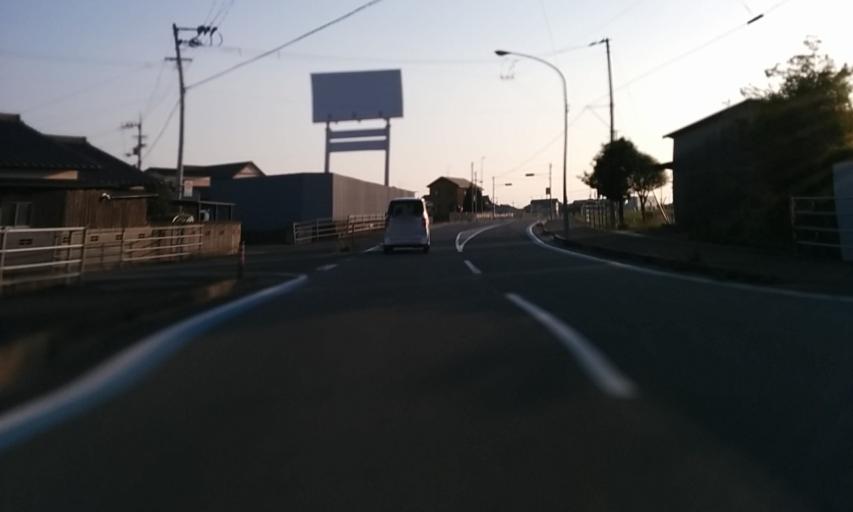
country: JP
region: Ehime
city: Masaki-cho
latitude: 33.7712
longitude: 132.7366
